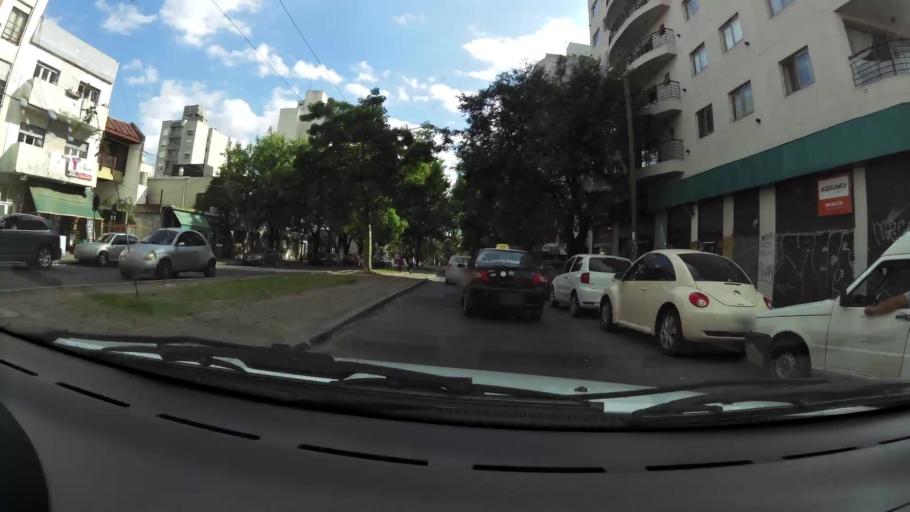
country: AR
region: Buenos Aires
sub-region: Partido de La Plata
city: La Plata
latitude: -34.9155
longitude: -57.9357
